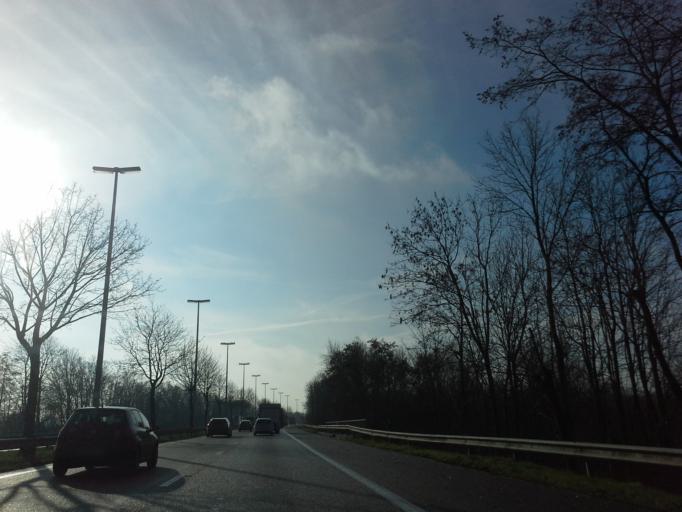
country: BE
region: Flanders
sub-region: Provincie Limburg
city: Hasselt
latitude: 50.9105
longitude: 5.3229
